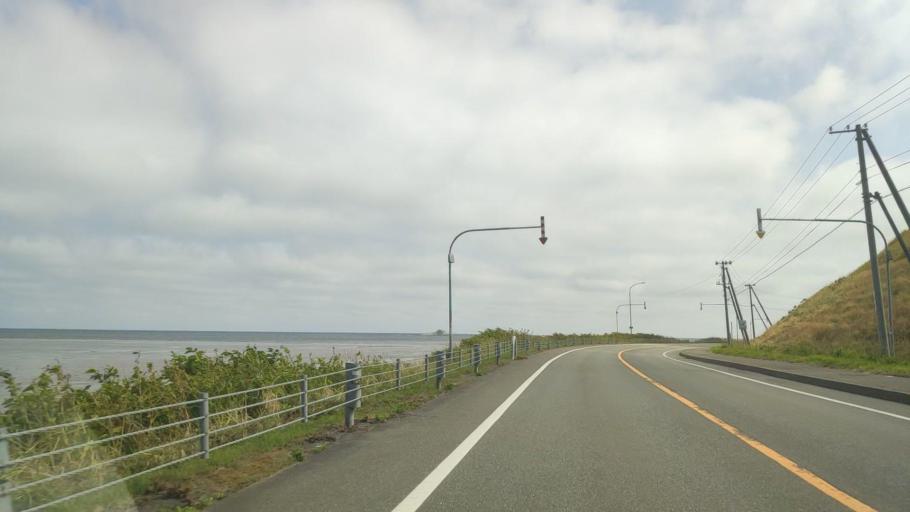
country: JP
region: Hokkaido
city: Makubetsu
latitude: 45.5167
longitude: 141.9111
